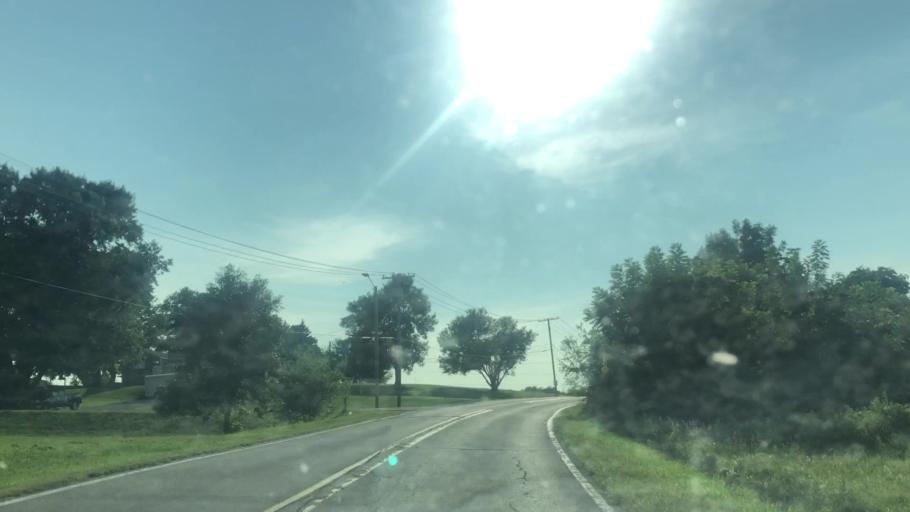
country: US
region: Iowa
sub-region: Marshall County
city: Marshalltown
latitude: 42.0523
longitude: -92.9545
